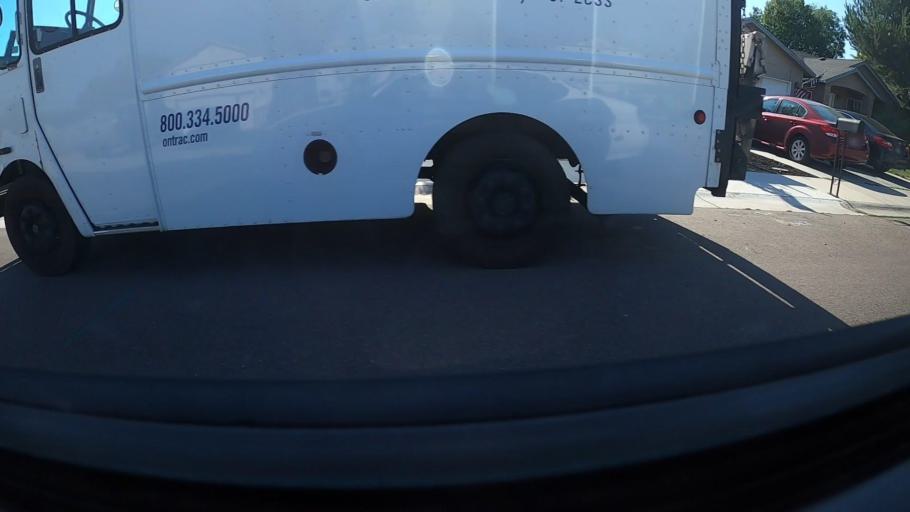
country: US
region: Idaho
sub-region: Ada County
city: Meridian
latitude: 43.6237
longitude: -116.3689
